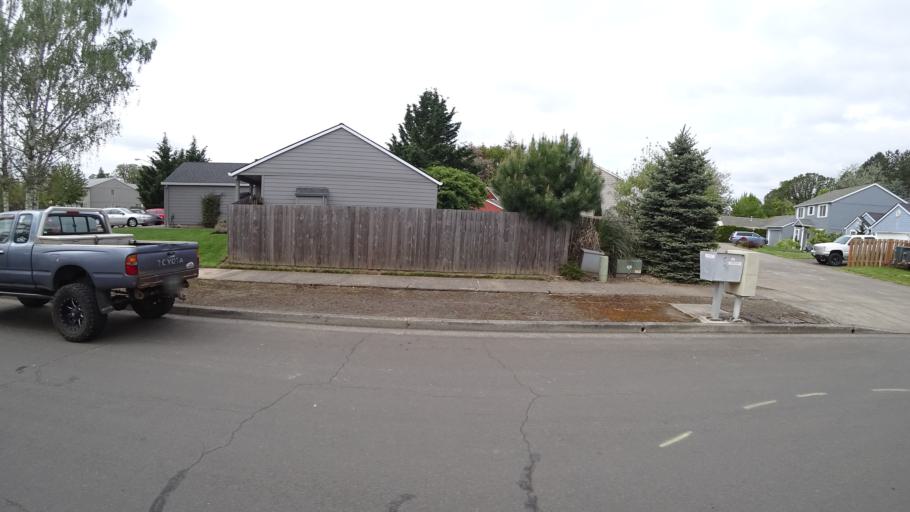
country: US
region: Oregon
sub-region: Washington County
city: Hillsboro
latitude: 45.5452
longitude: -122.9945
